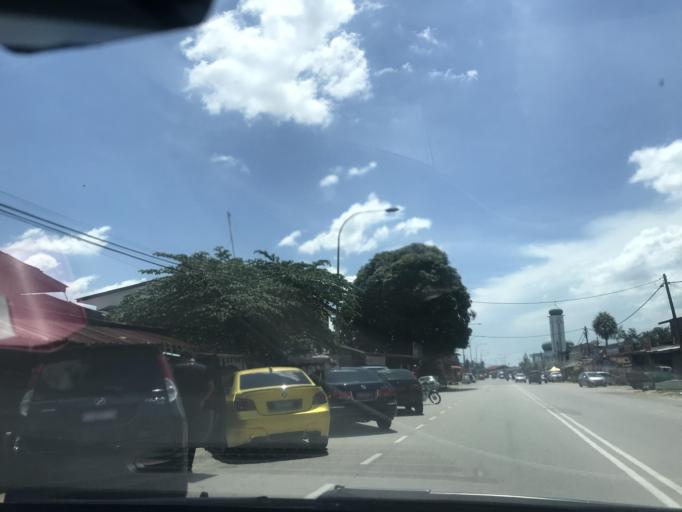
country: MY
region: Kelantan
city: Kota Bharu
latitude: 6.1135
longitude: 102.2659
